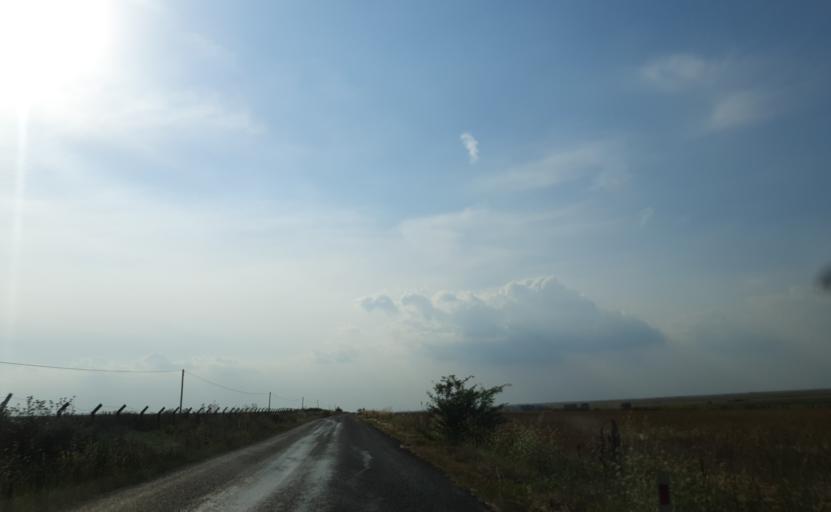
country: TR
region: Tekirdag
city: Muratli
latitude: 41.2087
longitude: 27.4537
